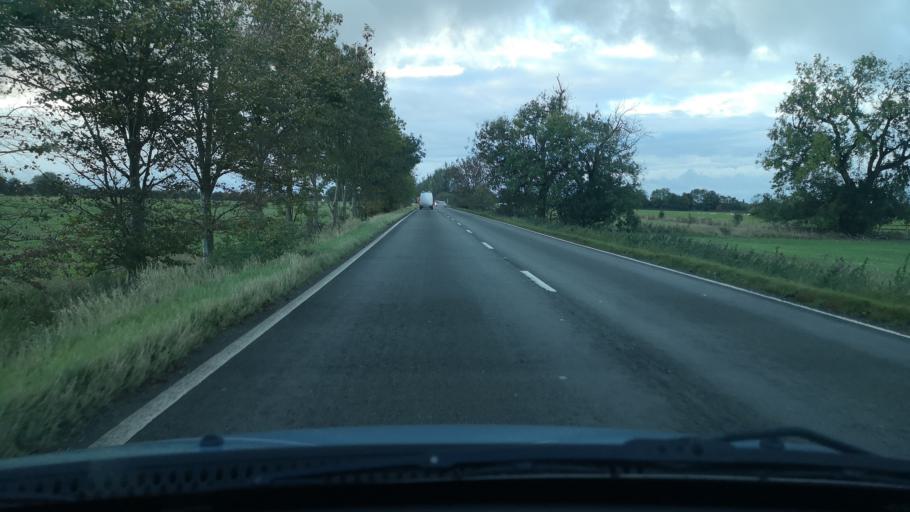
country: GB
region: England
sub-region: Doncaster
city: Hatfield
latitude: 53.5924
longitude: -0.9412
